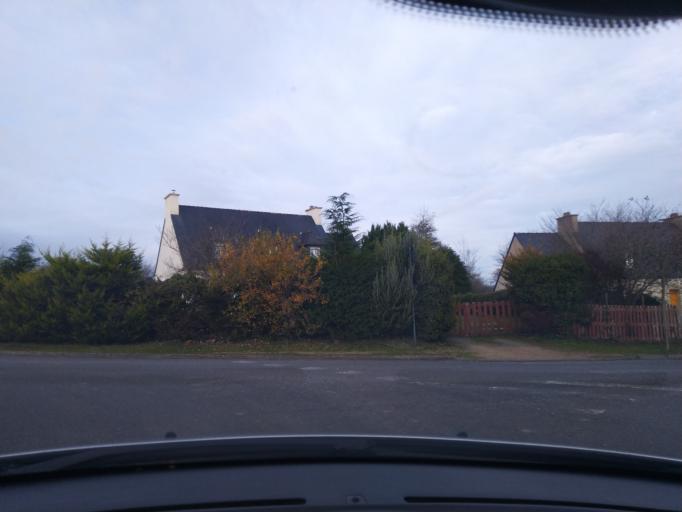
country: FR
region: Brittany
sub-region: Departement du Finistere
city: Guerlesquin
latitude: 48.5179
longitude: -3.5962
